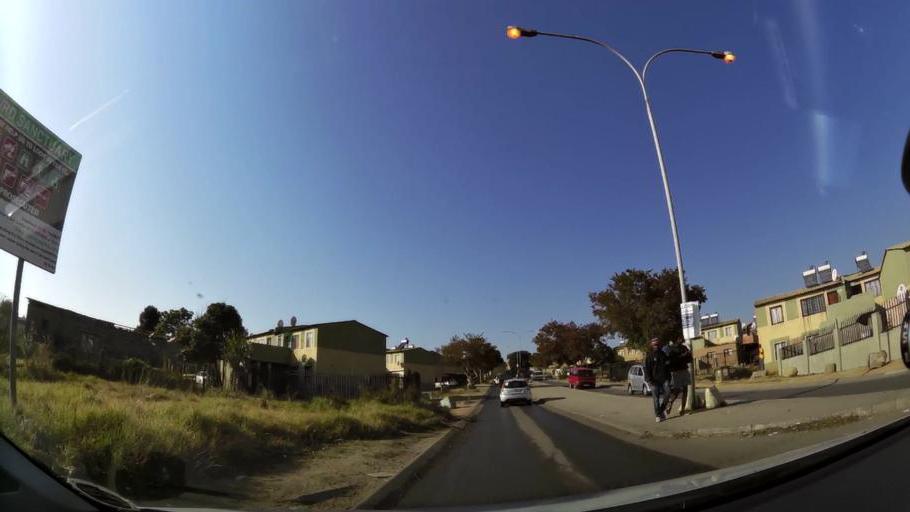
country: ZA
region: Gauteng
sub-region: City of Johannesburg Metropolitan Municipality
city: Modderfontein
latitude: -26.1011
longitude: 28.1179
